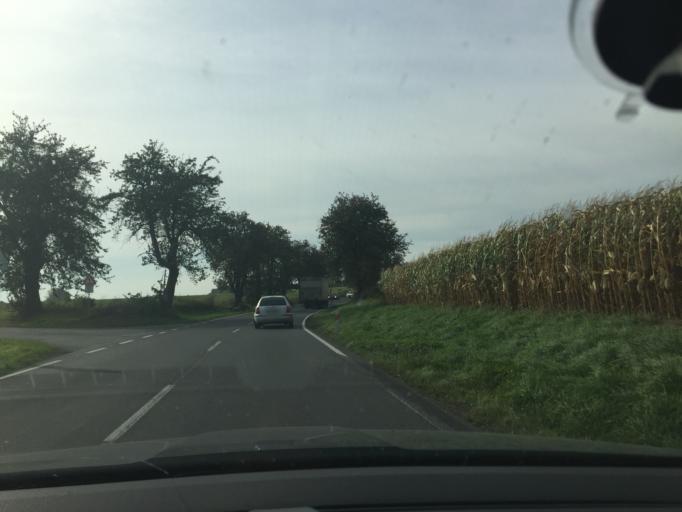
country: CZ
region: Central Bohemia
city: Cirkvice
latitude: 49.9424
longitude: 15.3262
